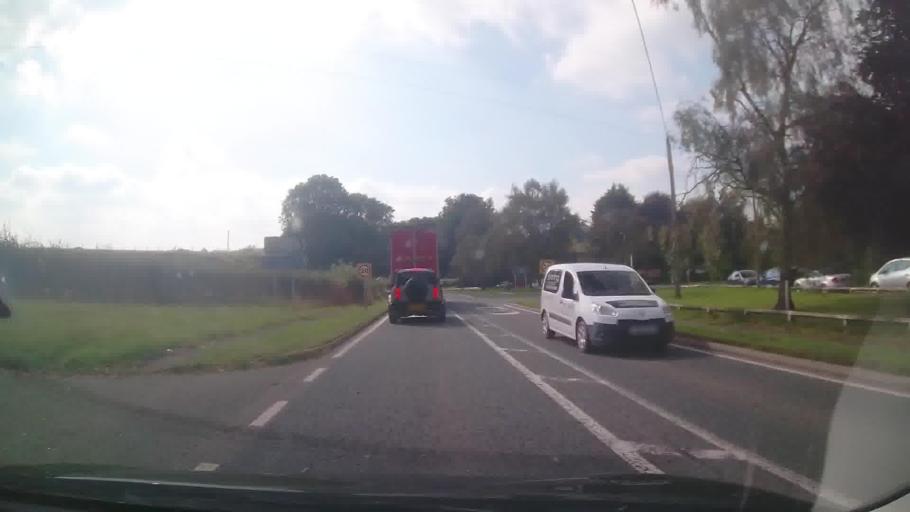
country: GB
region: England
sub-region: Cheshire West and Chester
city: Tiverton
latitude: 53.1378
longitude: -2.6671
